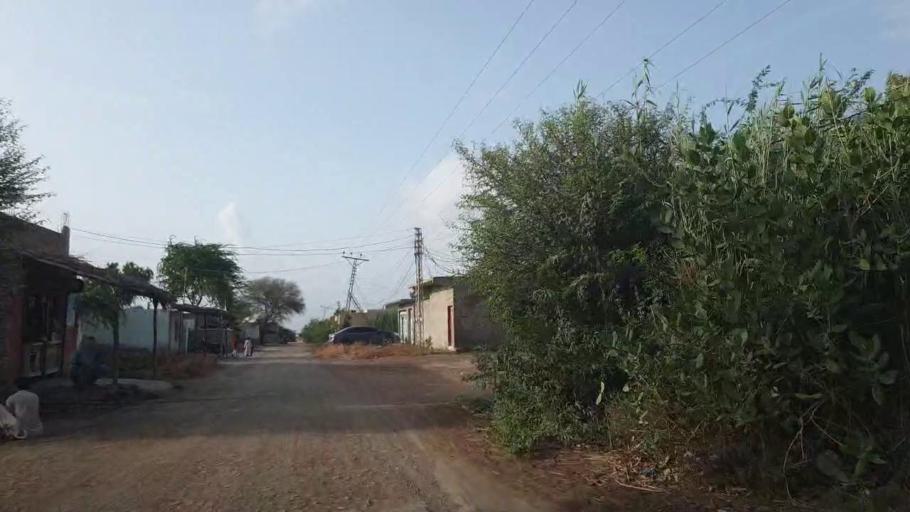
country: PK
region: Sindh
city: Tando Bago
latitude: 24.6450
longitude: 69.1118
